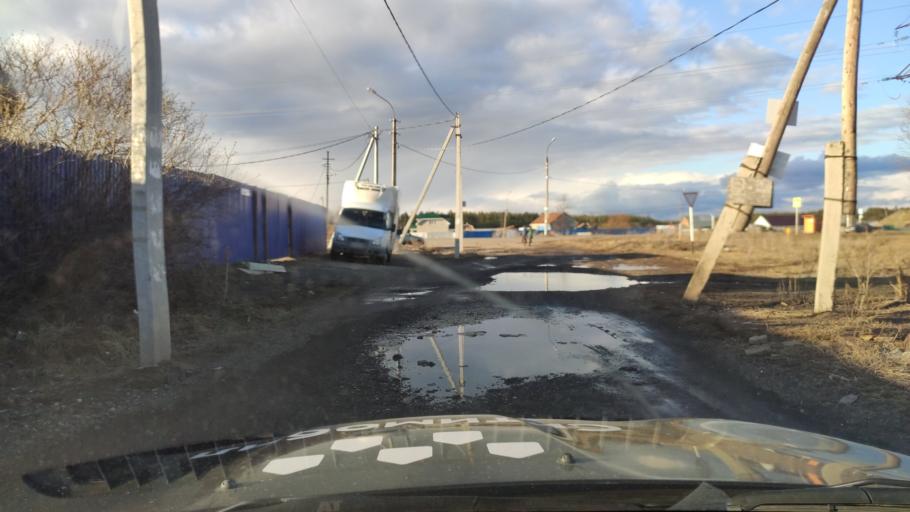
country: RU
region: Samara
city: Povolzhskiy
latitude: 53.5877
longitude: 49.7275
